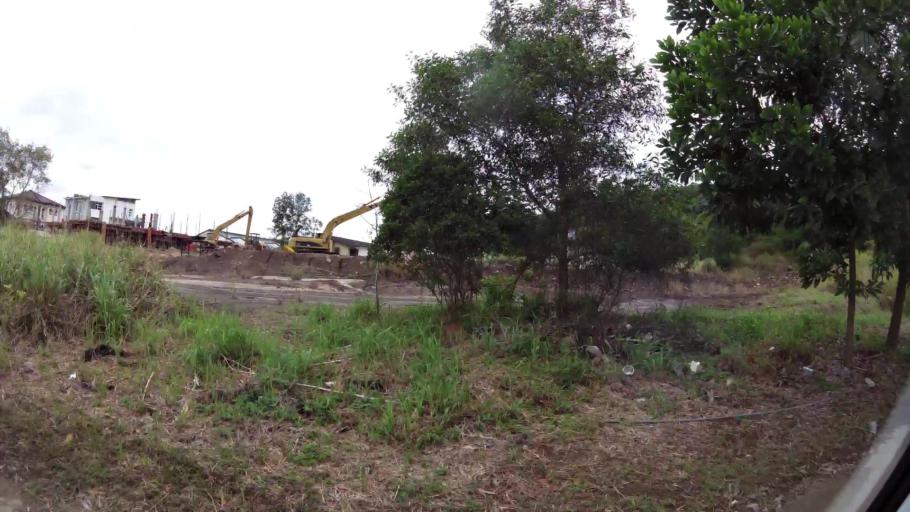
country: BN
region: Brunei and Muara
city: Bandar Seri Begawan
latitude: 4.8879
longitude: 114.9126
